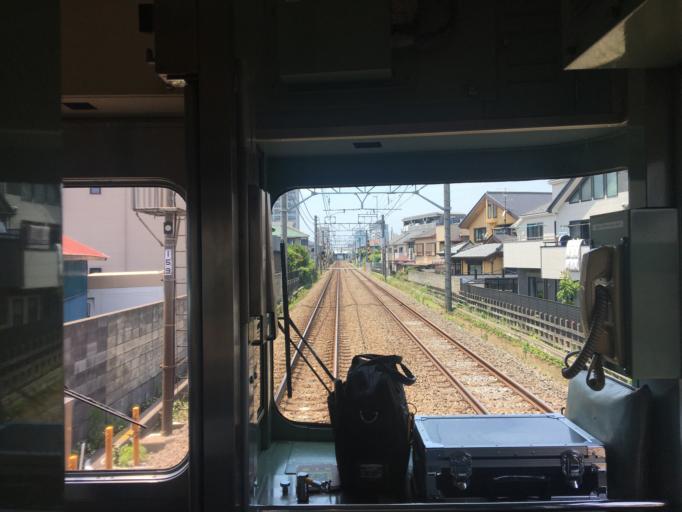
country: JP
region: Tokyo
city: Tanashicho
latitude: 35.7488
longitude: 139.5520
